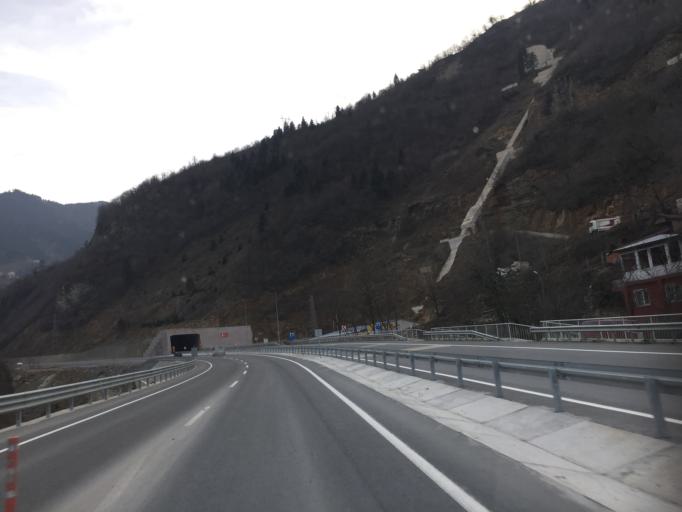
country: TR
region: Trabzon
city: Macka
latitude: 40.7592
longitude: 39.5630
